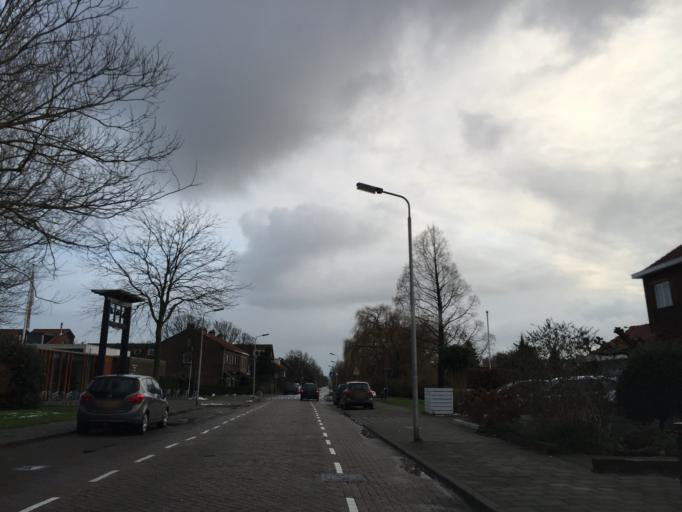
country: NL
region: South Holland
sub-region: Gemeente Pijnacker-Nootdorp
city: Pijnacker
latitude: 52.0091
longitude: 4.3960
